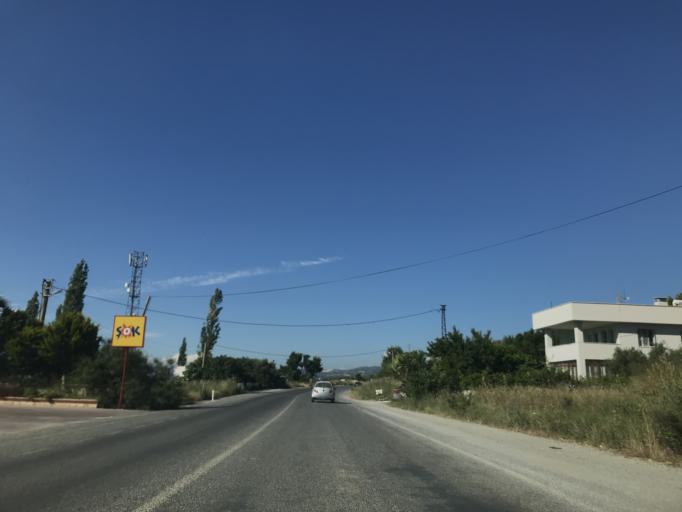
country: TR
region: Aydin
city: Davutlar
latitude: 37.7233
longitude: 27.2562
